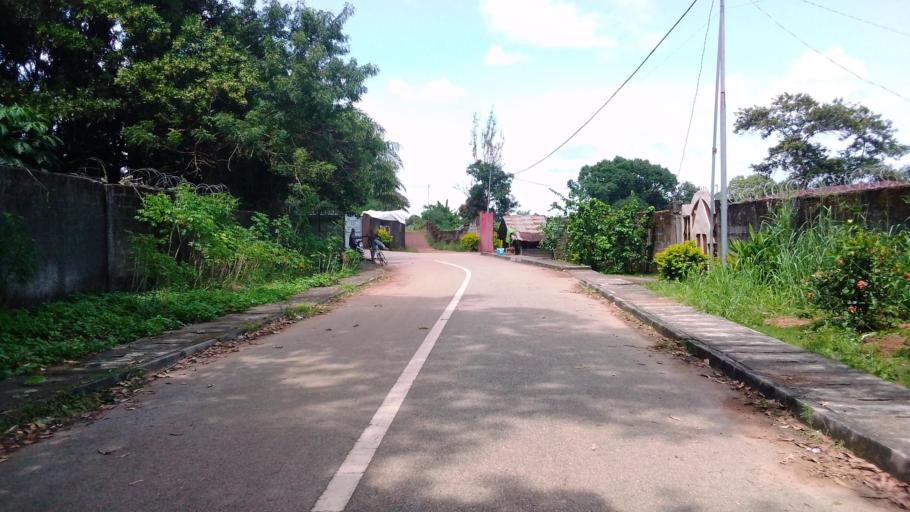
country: SL
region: Northern Province
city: Makeni
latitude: 8.8809
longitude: -12.0324
